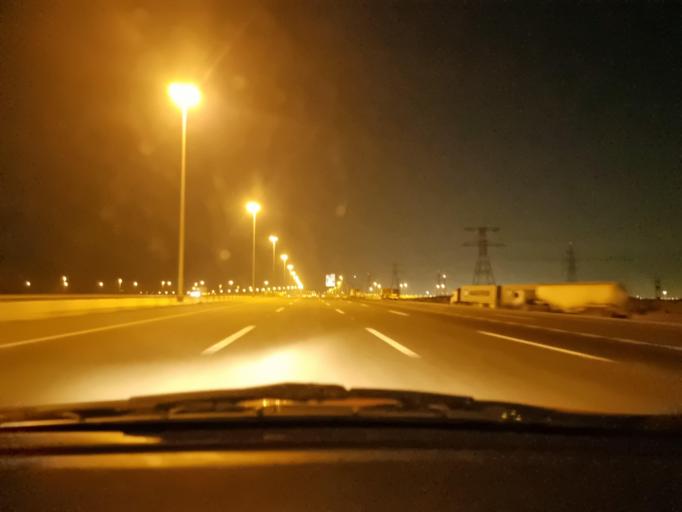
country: AE
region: Abu Dhabi
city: Abu Dhabi
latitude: 24.4722
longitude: 54.7498
